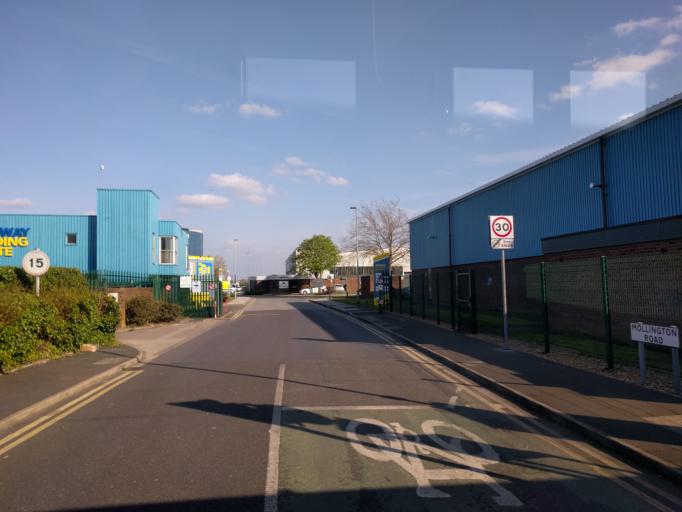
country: GB
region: England
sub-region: Manchester
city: Ringway
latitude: 53.3699
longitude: -2.2516
